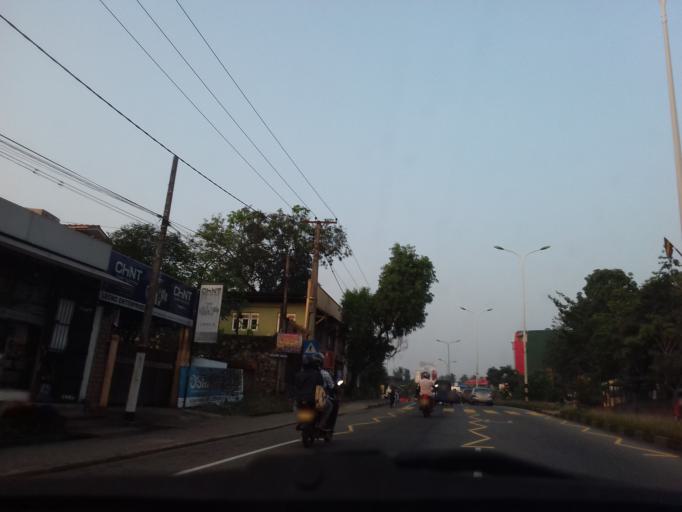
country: LK
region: Western
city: Kelaniya
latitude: 6.9895
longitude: 79.9380
